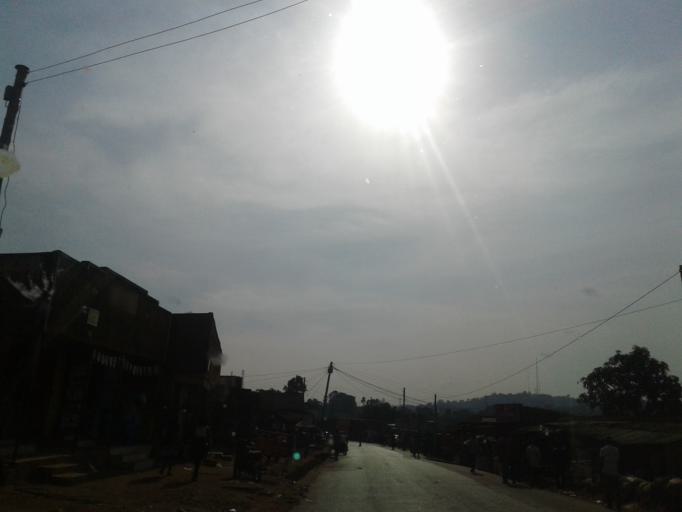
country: UG
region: Central Region
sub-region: Wakiso District
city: Kireka
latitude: 0.3331
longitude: 32.6248
